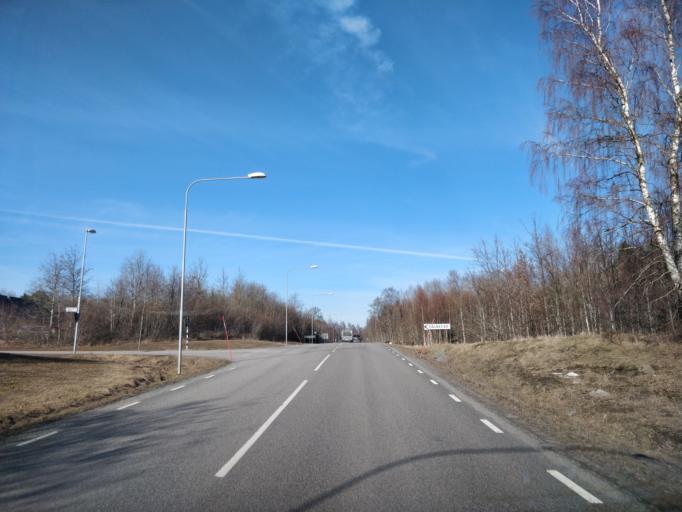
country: SE
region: Uppsala
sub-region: Enkopings Kommun
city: Orsundsbro
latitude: 59.7410
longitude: 17.3321
